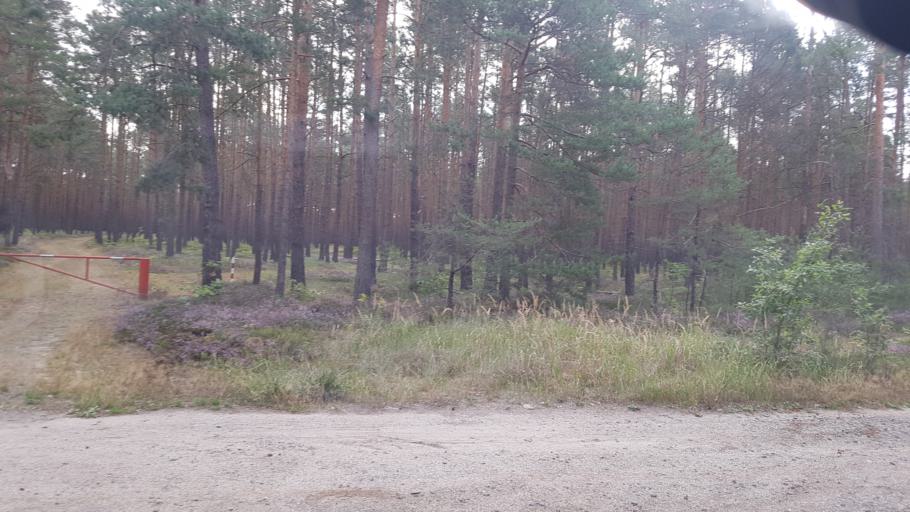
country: DE
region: Brandenburg
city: Ruckersdorf
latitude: 51.5764
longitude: 13.5985
